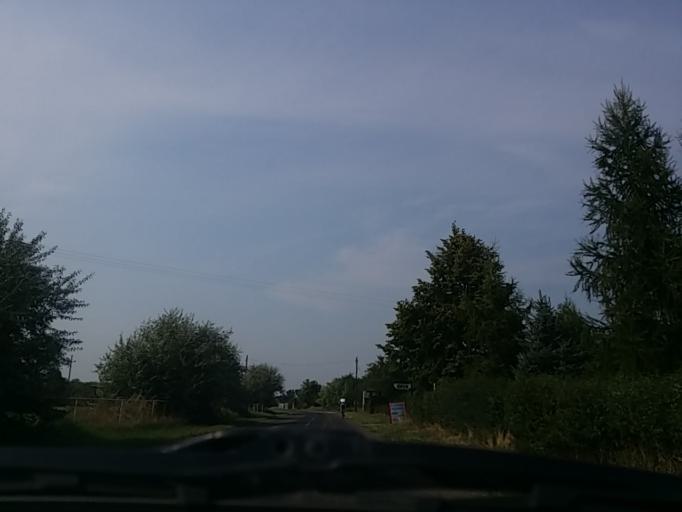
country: HU
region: Komarom-Esztergom
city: Oroszlany
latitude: 47.5000
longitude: 18.3690
